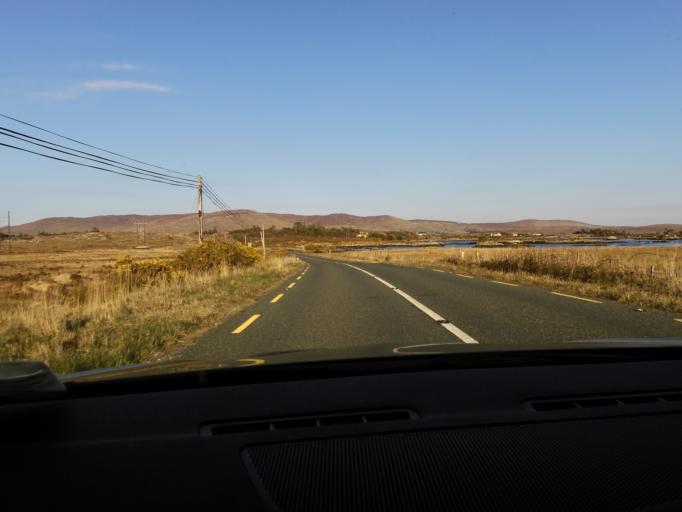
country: IE
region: Connaught
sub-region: County Galway
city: Oughterard
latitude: 53.3840
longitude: -9.5679
